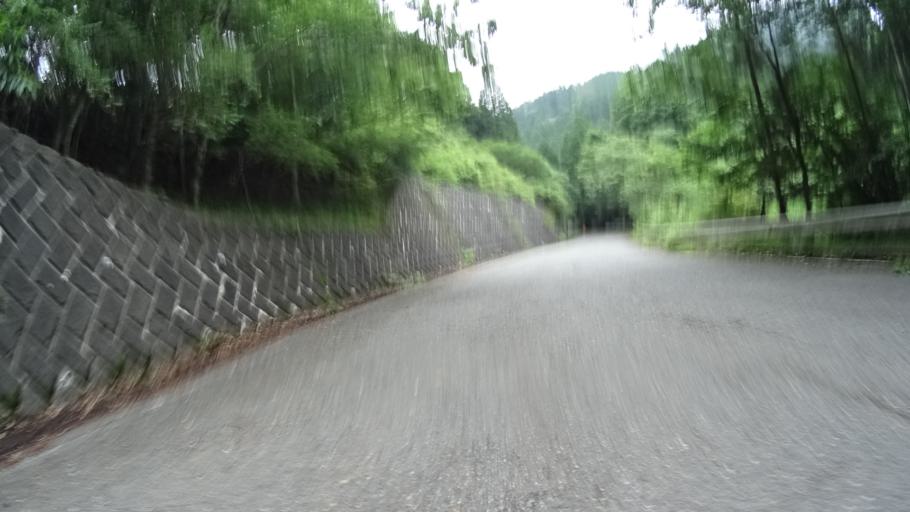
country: JP
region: Kanagawa
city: Hadano
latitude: 35.4335
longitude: 139.2109
